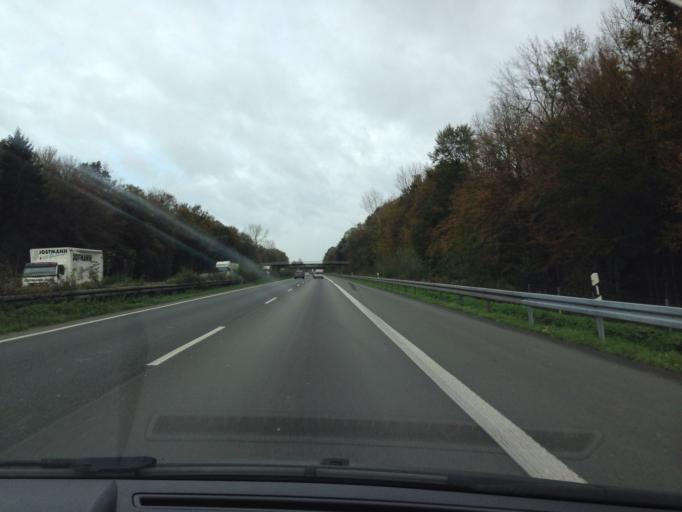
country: DE
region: North Rhine-Westphalia
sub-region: Regierungsbezirk Munster
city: Ascheberg
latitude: 51.8267
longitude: 7.6041
